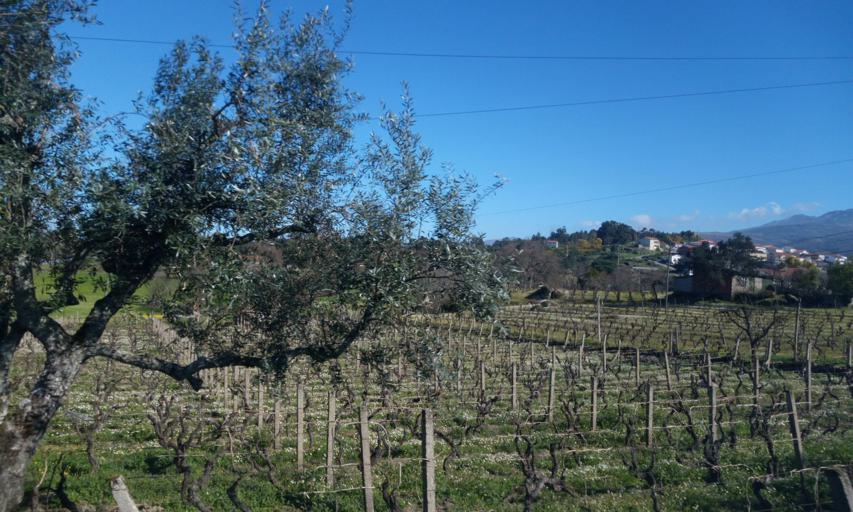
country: PT
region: Guarda
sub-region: Fornos de Algodres
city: Fornos de Algodres
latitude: 40.5203
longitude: -7.6132
